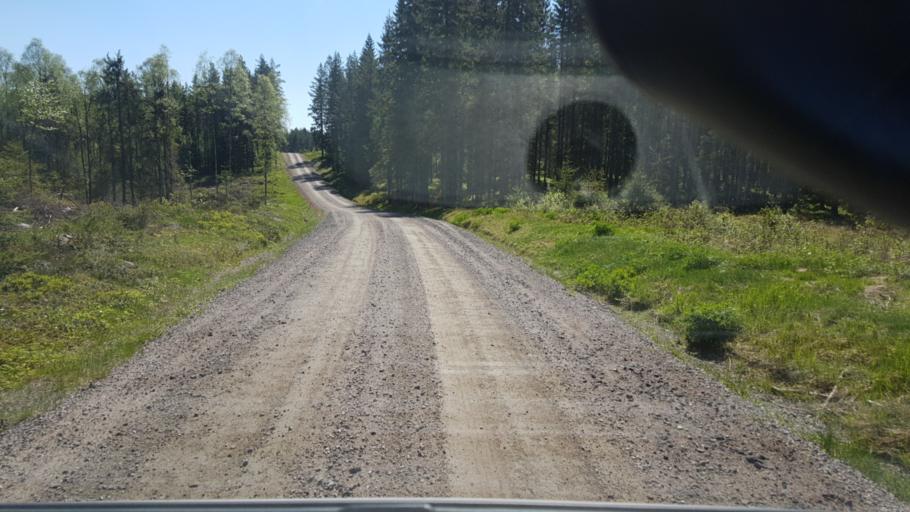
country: SE
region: Vaermland
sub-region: Eda Kommun
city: Charlottenberg
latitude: 60.0606
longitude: 12.5266
